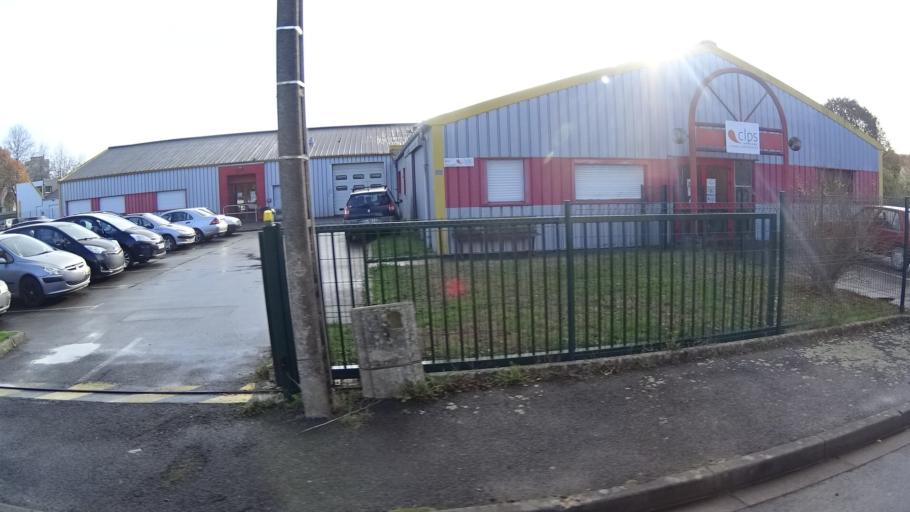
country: FR
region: Brittany
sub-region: Departement d'Ille-et-Vilaine
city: Redon
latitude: 47.6635
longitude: -2.0754
